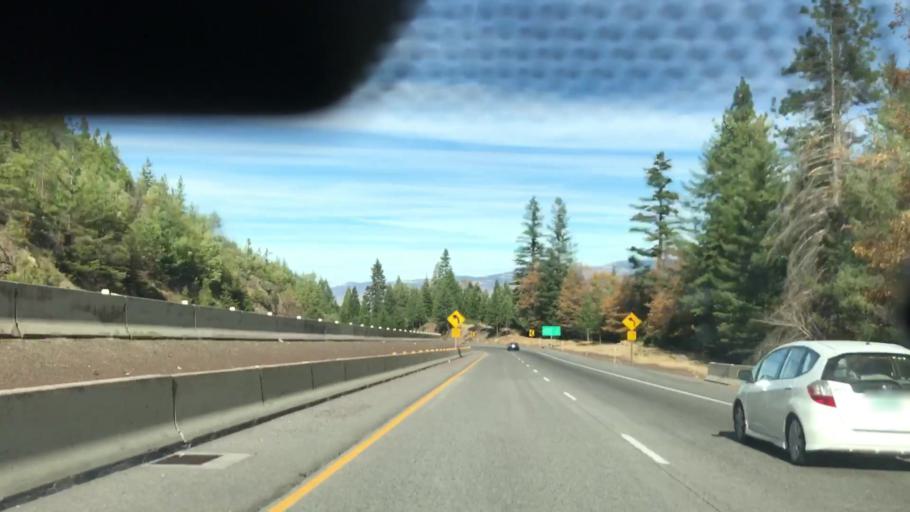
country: US
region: Oregon
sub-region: Jackson County
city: Ashland
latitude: 42.0921
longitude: -122.6028
